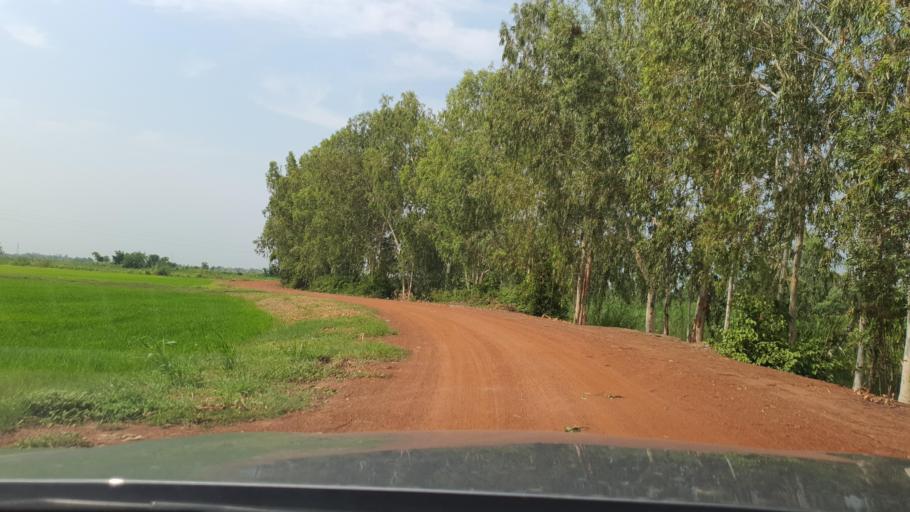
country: TH
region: Phitsanulok
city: Bang Rakam
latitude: 16.7864
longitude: 100.1083
